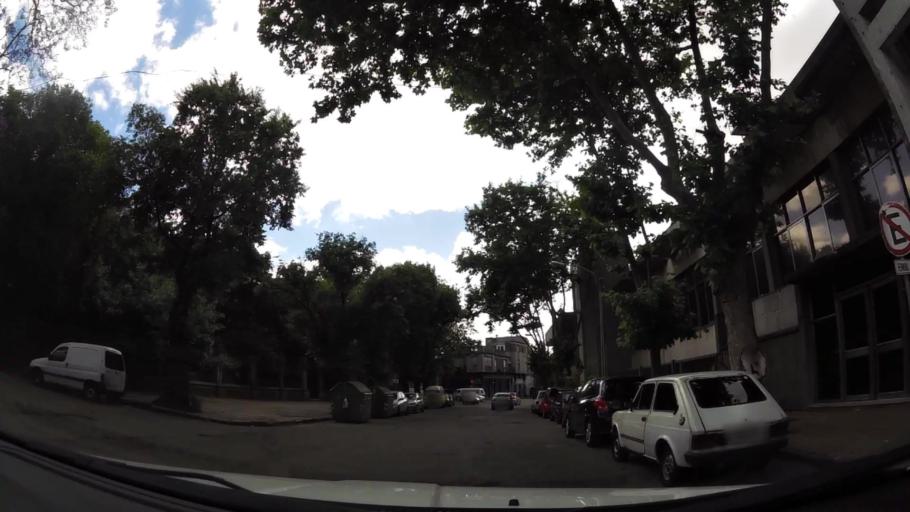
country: UY
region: Montevideo
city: Montevideo
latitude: -34.8763
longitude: -56.1864
